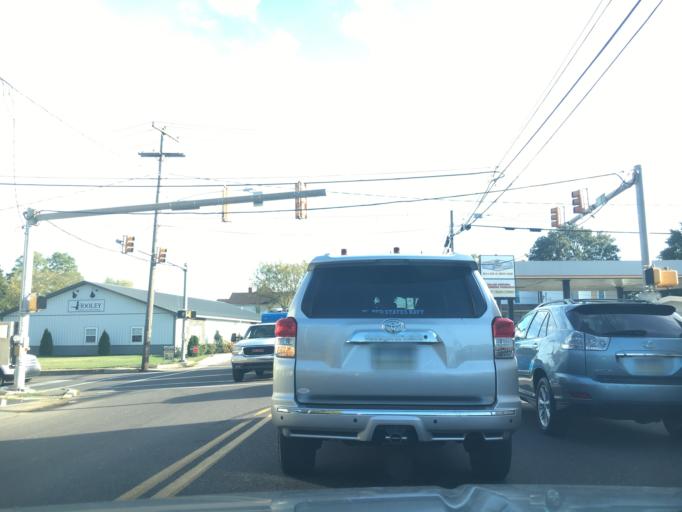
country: US
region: Pennsylvania
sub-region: Lancaster County
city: Brownstown
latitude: 40.1255
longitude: -76.2143
